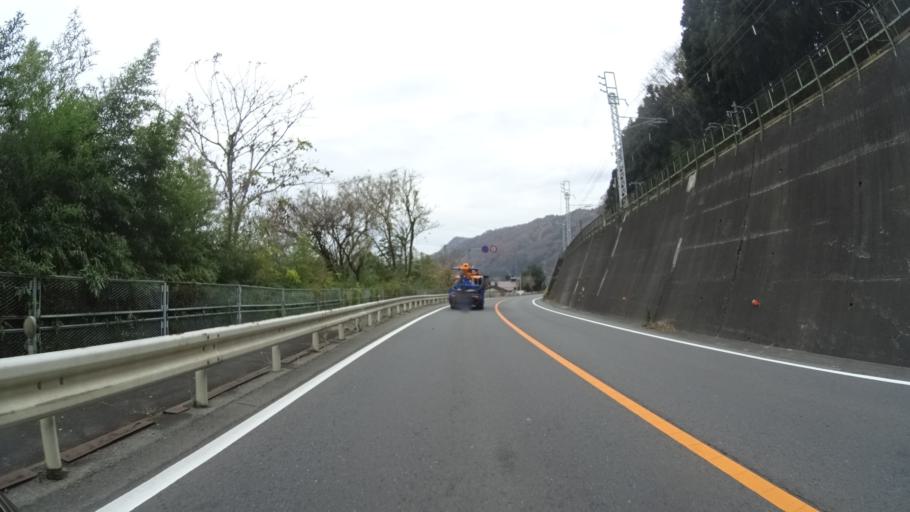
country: JP
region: Gunma
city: Numata
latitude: 36.6161
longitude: 139.0421
